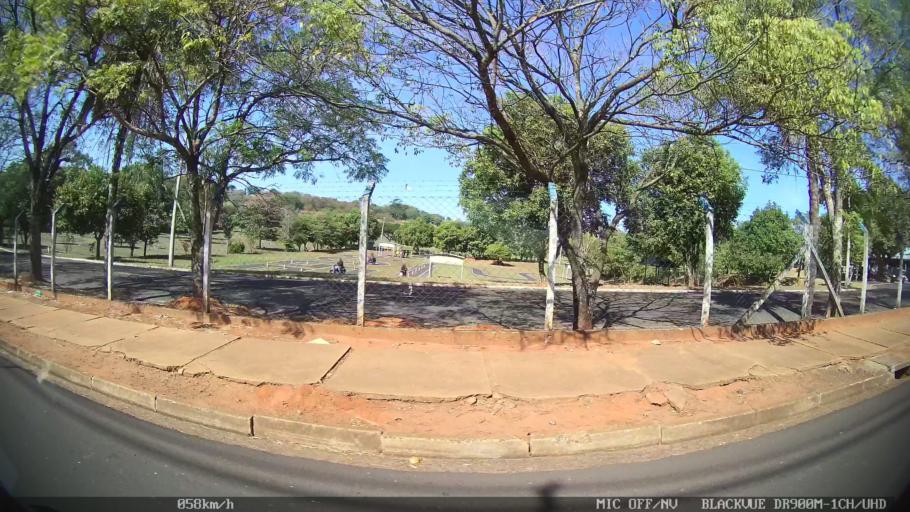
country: BR
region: Sao Paulo
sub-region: Sao Jose Do Rio Preto
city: Sao Jose do Rio Preto
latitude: -20.8109
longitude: -49.4171
